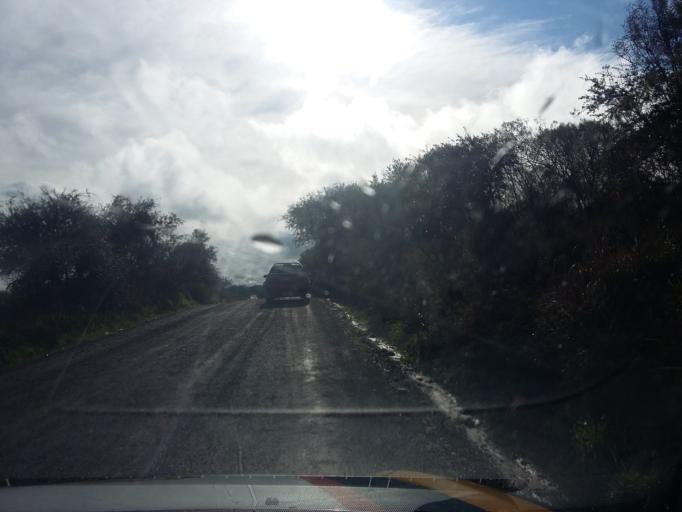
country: BR
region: Rio Grande do Sul
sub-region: Vacaria
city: Vacaria
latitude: -28.5331
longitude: -50.7987
